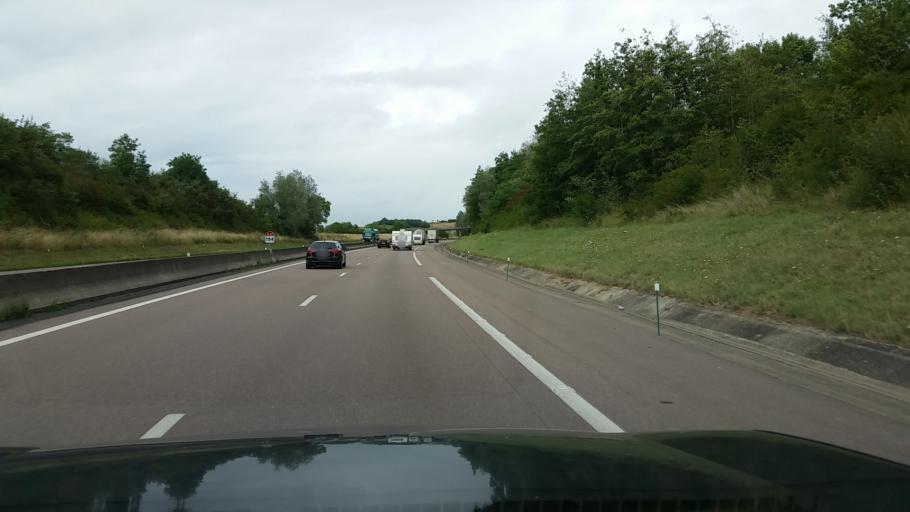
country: FR
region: Lorraine
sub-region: Departement des Vosges
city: Chatenois
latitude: 48.3680
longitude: 5.8702
